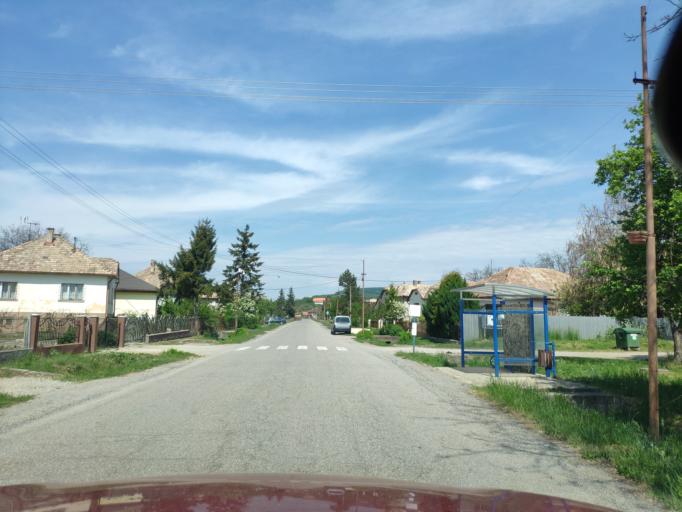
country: SK
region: Banskobystricky
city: Rimavska Sobota
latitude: 48.4409
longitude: 20.1149
